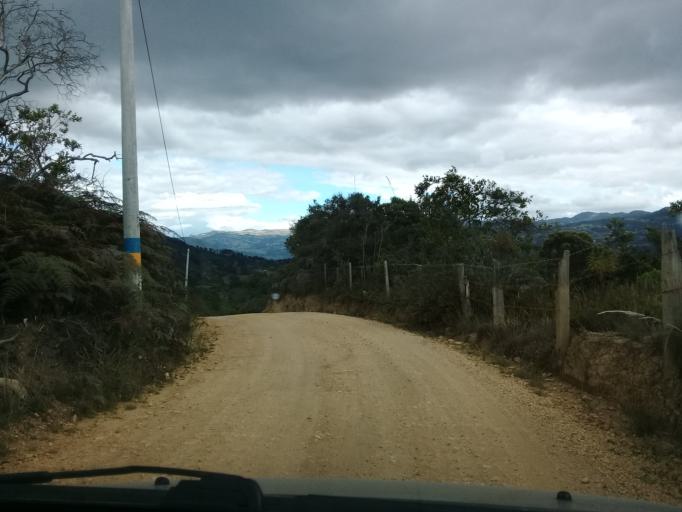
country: CO
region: Cundinamarca
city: Lenguazaque
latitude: 5.2842
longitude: -73.7408
